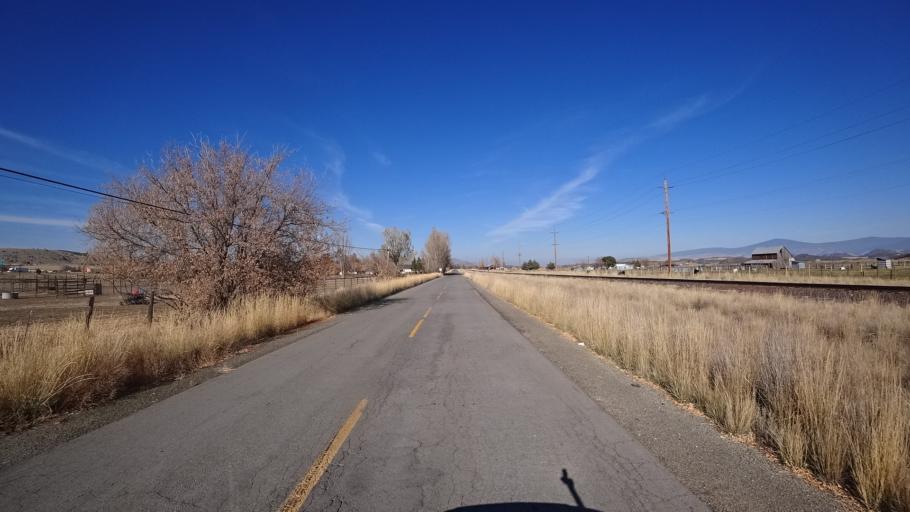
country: US
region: California
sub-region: Siskiyou County
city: Montague
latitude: 41.6302
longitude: -122.5219
